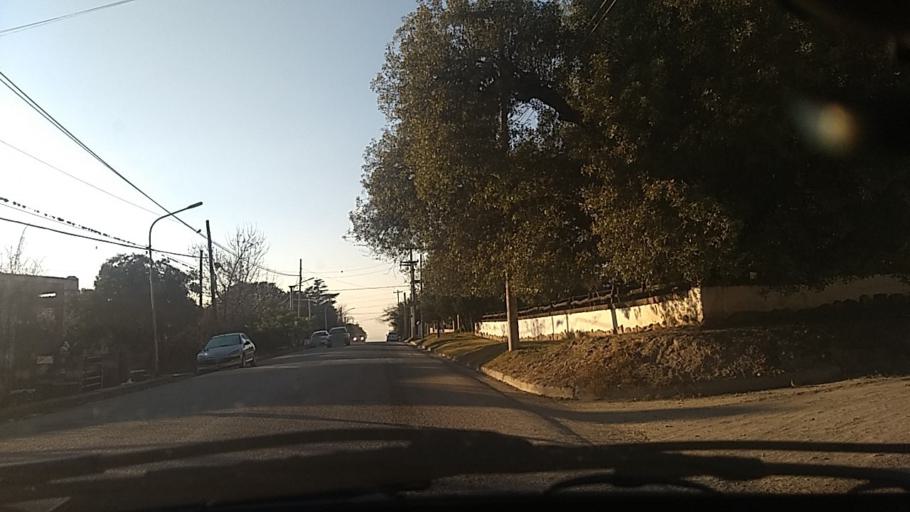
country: AR
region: Cordoba
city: Salsipuedes
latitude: -31.1398
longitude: -64.2895
